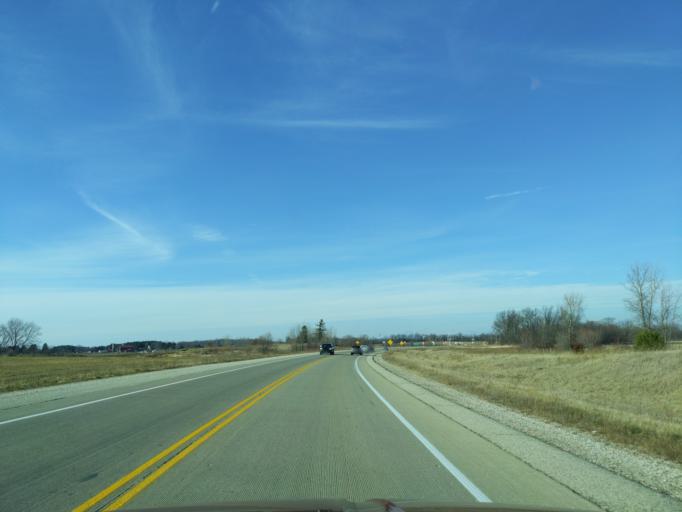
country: US
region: Wisconsin
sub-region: Walworth County
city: Whitewater
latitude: 42.8236
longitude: -88.7667
